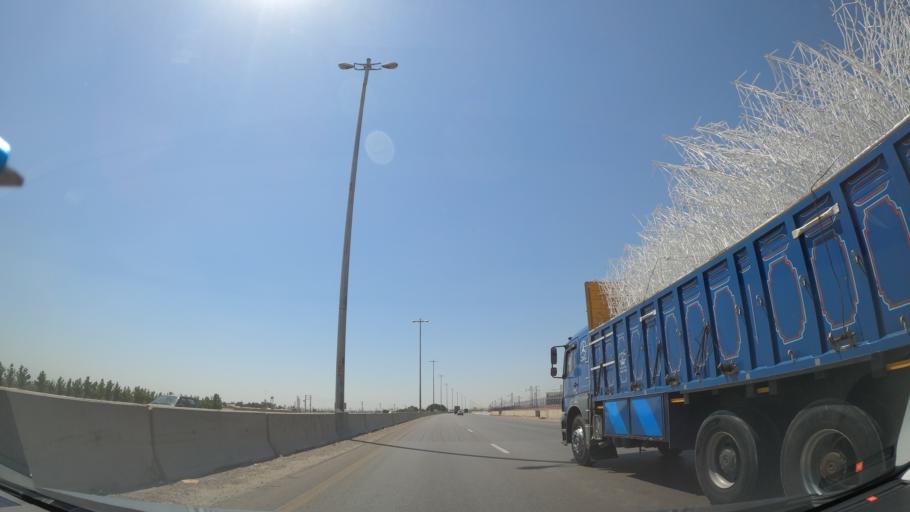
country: IR
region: Alborz
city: Hashtgerd
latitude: 35.9182
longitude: 50.7882
